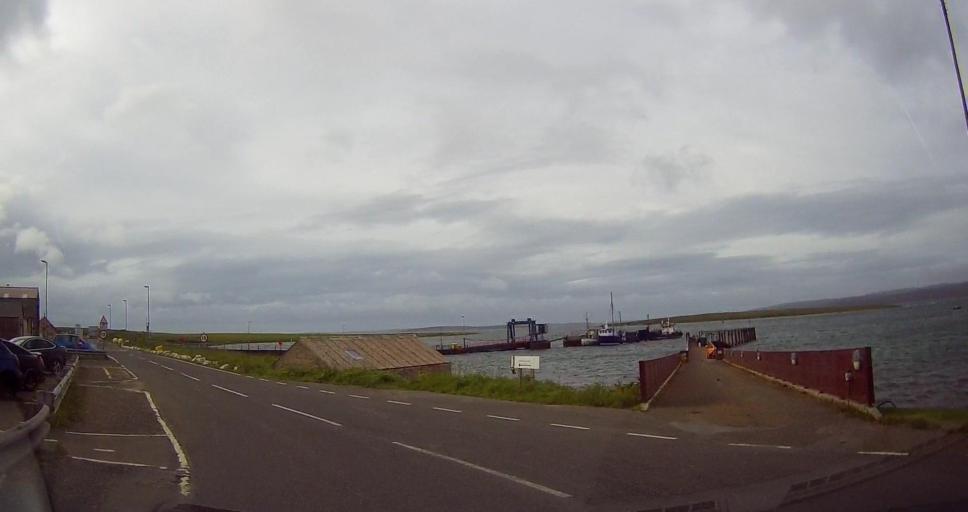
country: GB
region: Scotland
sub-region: Orkney Islands
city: Stromness
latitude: 58.9185
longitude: -3.1848
